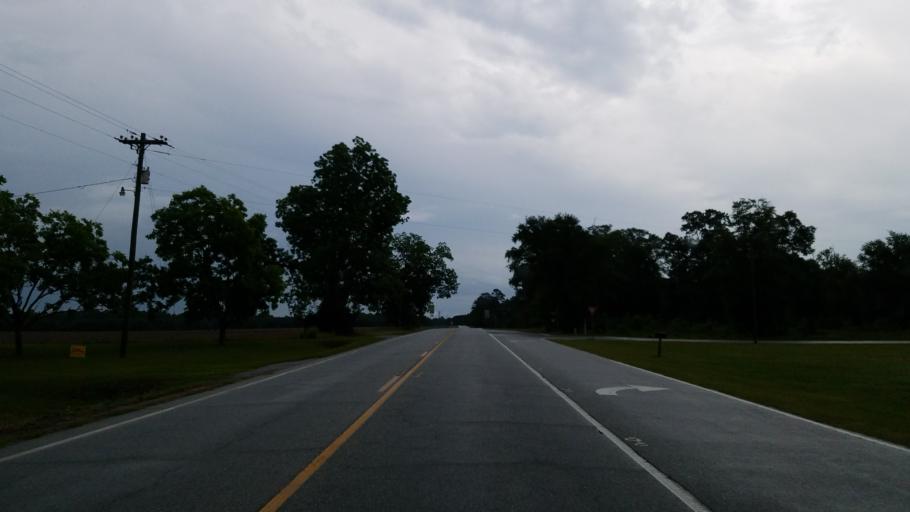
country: US
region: Georgia
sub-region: Cook County
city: Adel
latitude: 31.1346
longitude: -83.3820
